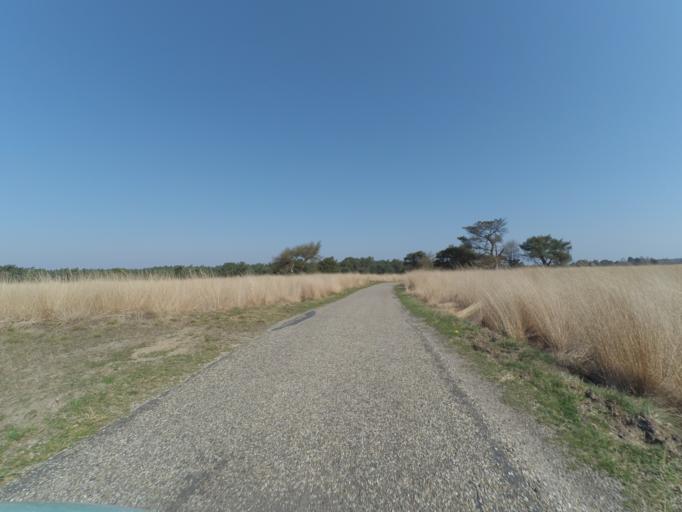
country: NL
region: Gelderland
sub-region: Gemeente Ede
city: Otterlo
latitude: 52.0886
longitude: 5.8521
